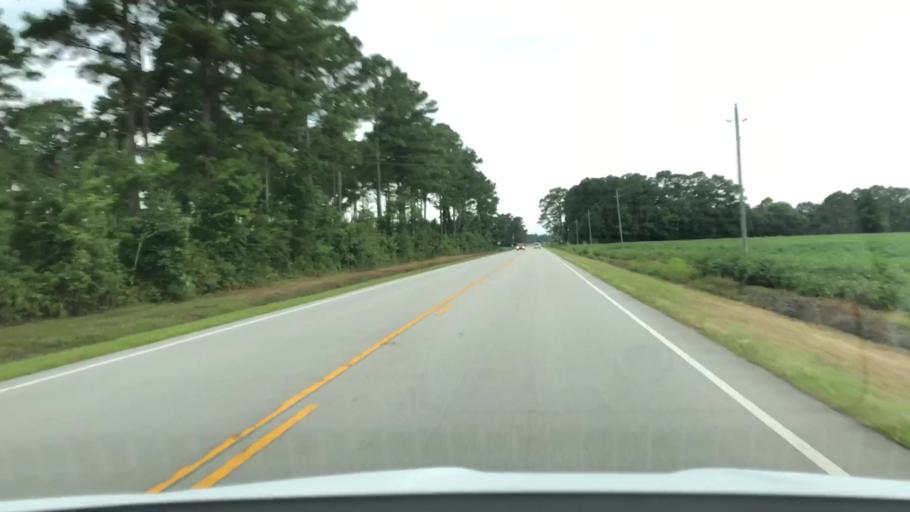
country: US
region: North Carolina
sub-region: Jones County
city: Trenton
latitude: 35.0746
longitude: -77.3872
